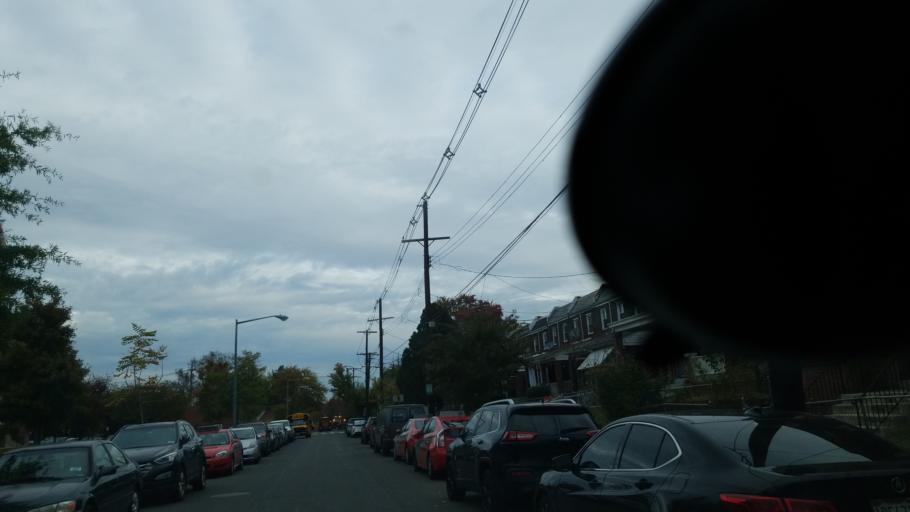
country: US
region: Maryland
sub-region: Prince George's County
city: Hillcrest Heights
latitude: 38.8697
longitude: -76.9822
